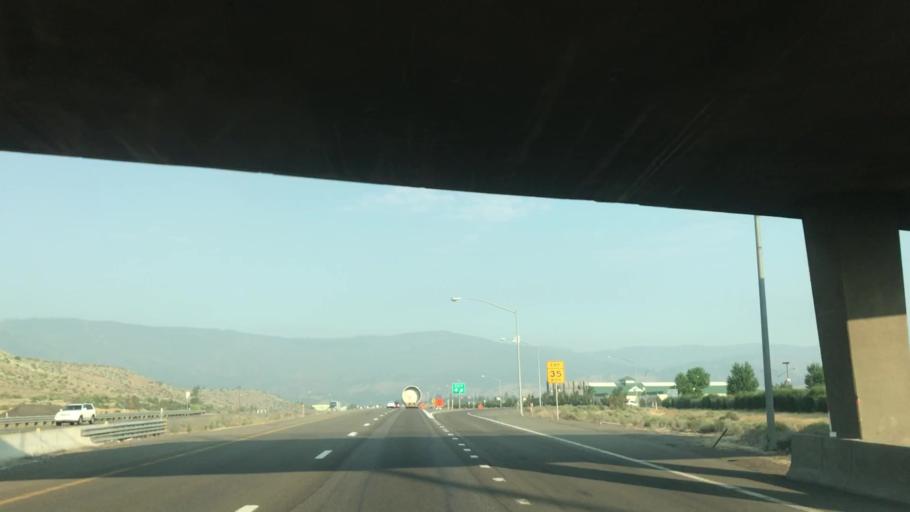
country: US
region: Nevada
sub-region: Washoe County
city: Verdi
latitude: 39.5110
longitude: -119.9643
